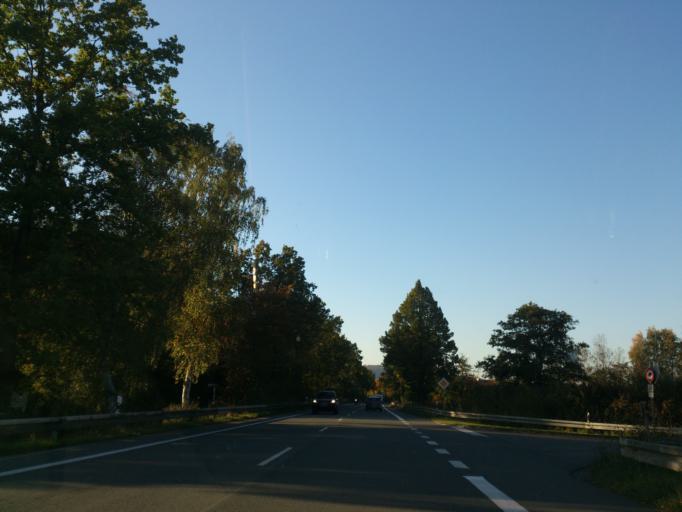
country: DE
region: North Rhine-Westphalia
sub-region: Regierungsbezirk Detmold
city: Willebadessen
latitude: 51.6197
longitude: 9.0297
